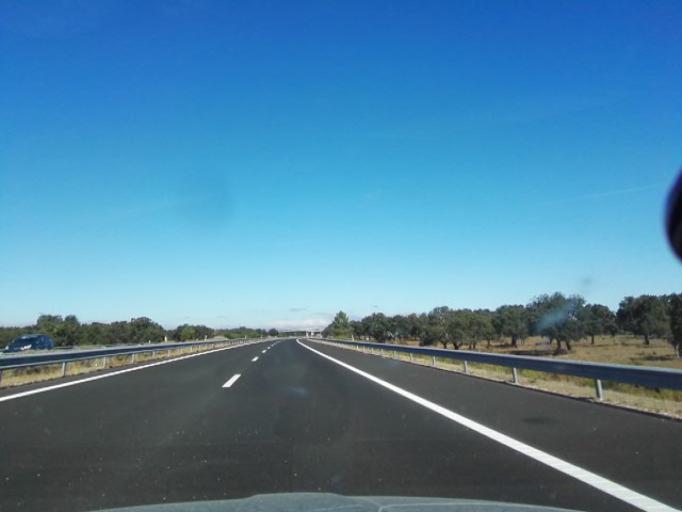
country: PT
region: Santarem
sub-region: Benavente
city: Benavente
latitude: 38.9198
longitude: -8.8065
